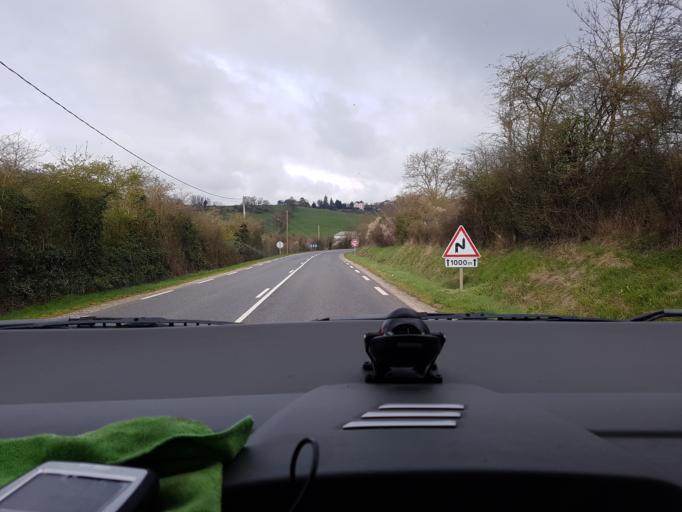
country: FR
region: Midi-Pyrenees
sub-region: Departement de l'Aveyron
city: Olemps
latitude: 44.3656
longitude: 2.5441
